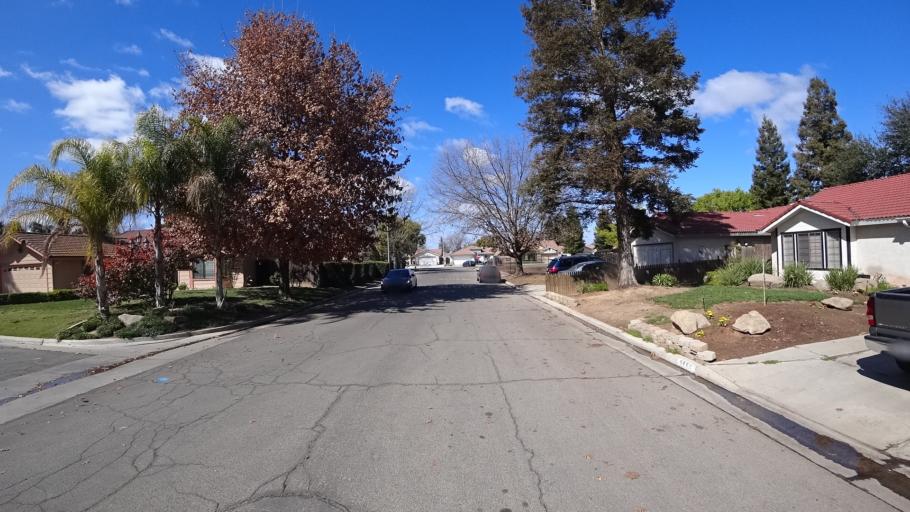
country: US
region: California
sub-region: Fresno County
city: West Park
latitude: 36.8241
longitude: -119.8932
